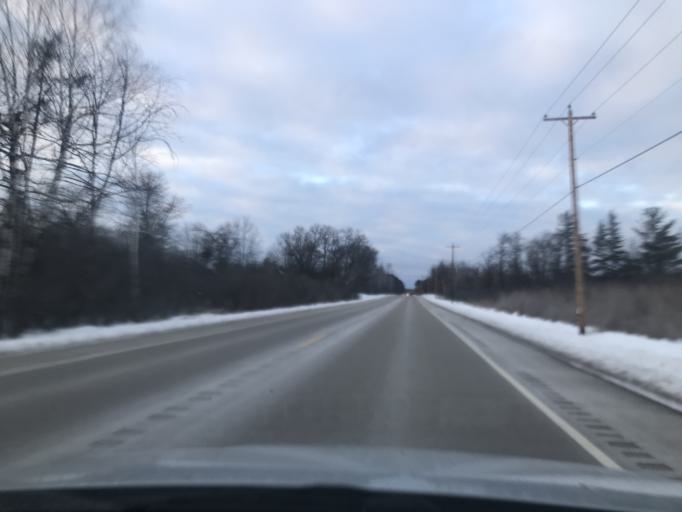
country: US
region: Wisconsin
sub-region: Marinette County
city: Marinette
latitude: 45.1230
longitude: -87.6837
